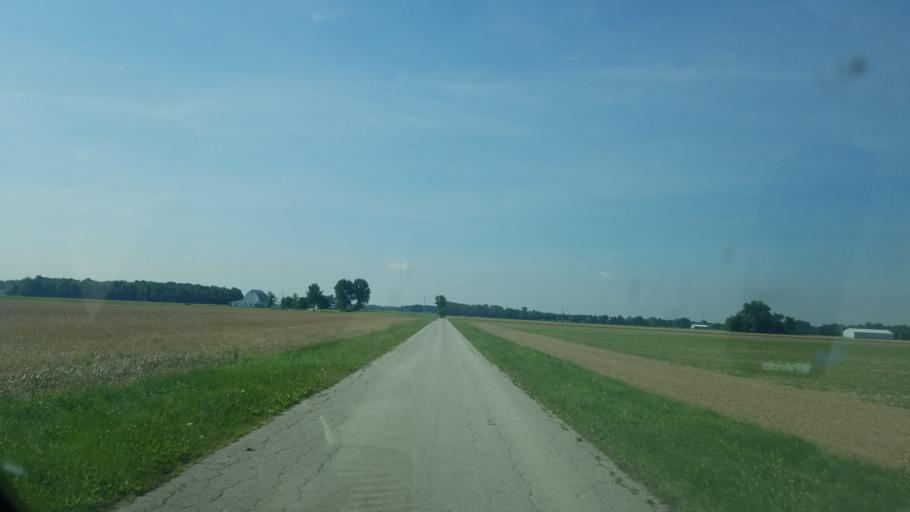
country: US
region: Ohio
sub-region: Wyandot County
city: Carey
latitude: 40.9814
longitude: -83.3193
